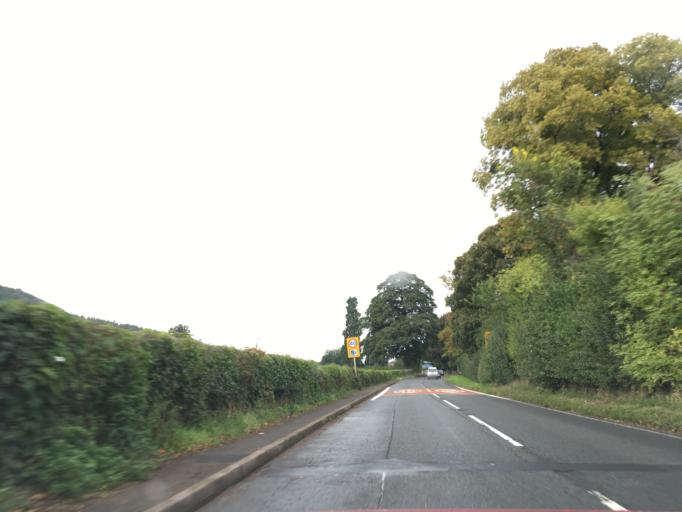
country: GB
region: England
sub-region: Herefordshire
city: Ross on Wye
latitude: 51.9084
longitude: -2.5391
